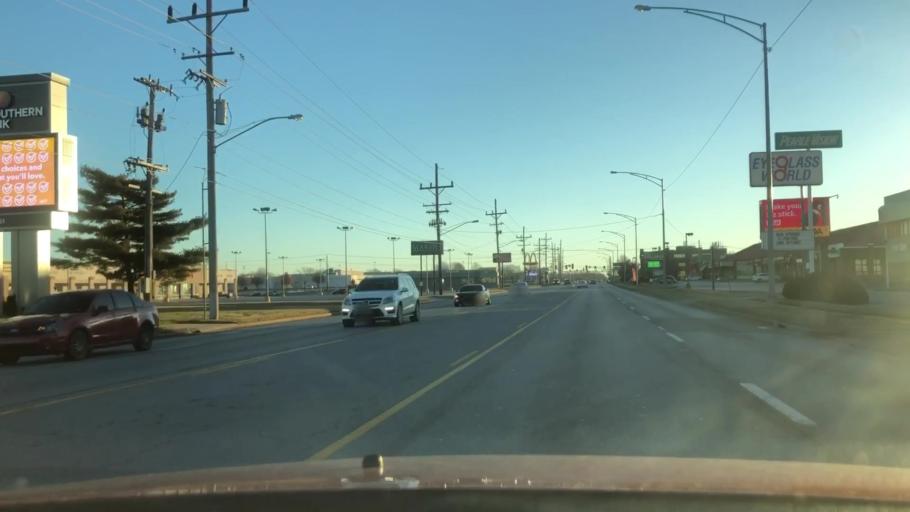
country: US
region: Missouri
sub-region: Greene County
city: Springfield
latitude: 37.1595
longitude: -93.2703
